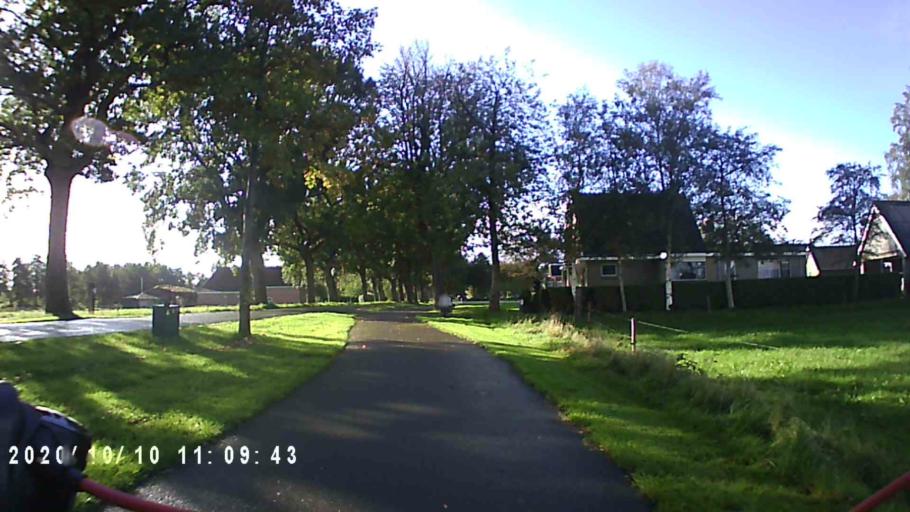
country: NL
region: Friesland
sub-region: Gemeente Smallingerland
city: Drachtstercompagnie
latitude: 53.1178
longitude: 6.2071
